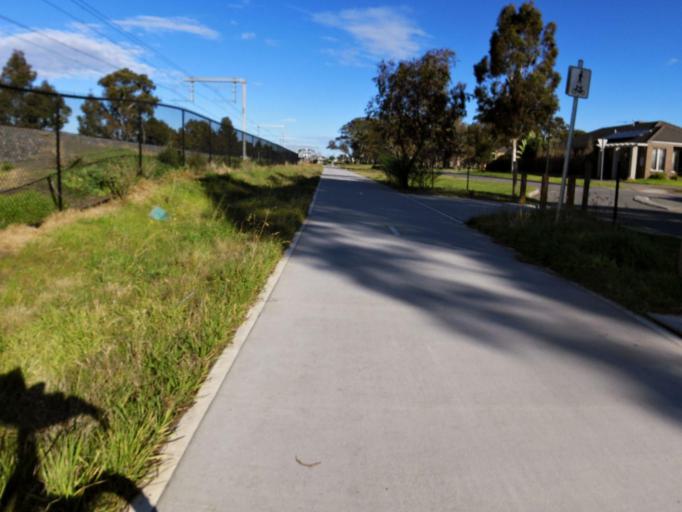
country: AU
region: Victoria
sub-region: Whittlesea
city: Mernda
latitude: -37.6170
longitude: 145.0976
